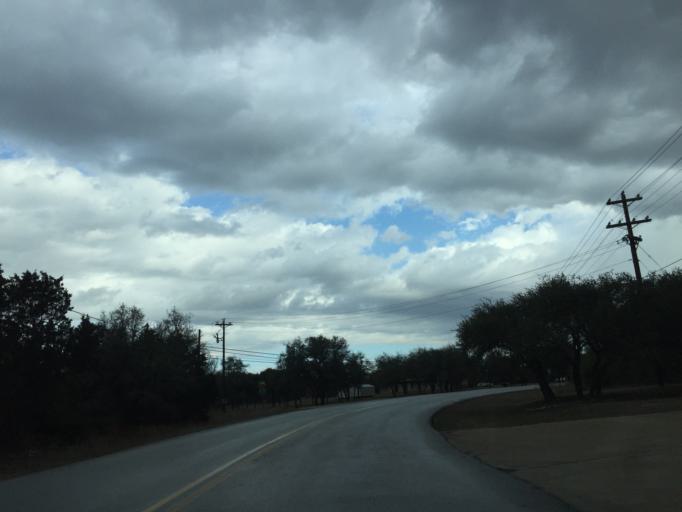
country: US
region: Texas
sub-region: Travis County
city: Jonestown
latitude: 30.5731
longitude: -97.9493
